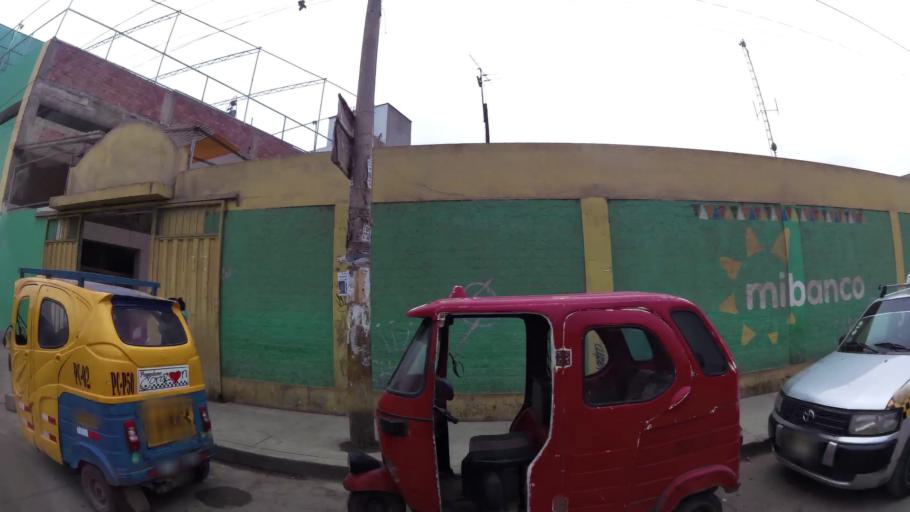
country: PE
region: Lima
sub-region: Lima
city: La Molina
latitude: -12.1320
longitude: -76.9549
